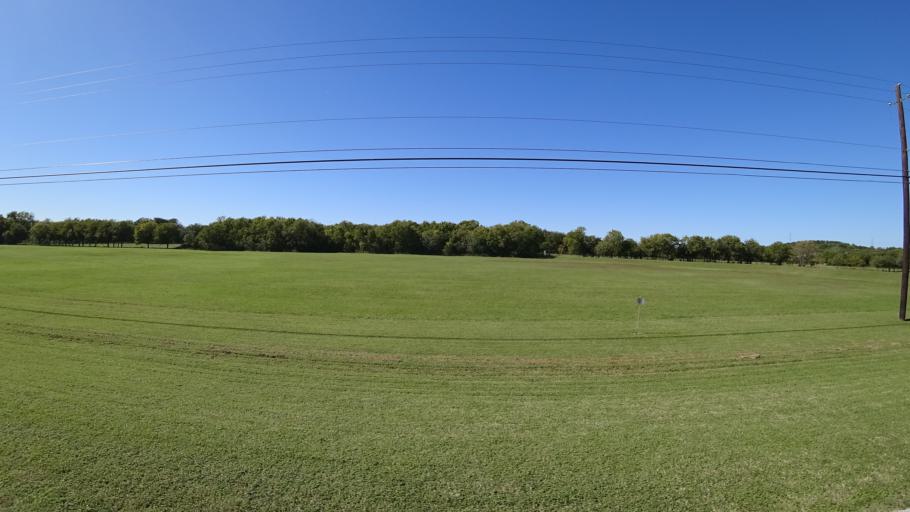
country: US
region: Texas
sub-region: Travis County
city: Hornsby Bend
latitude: 30.2747
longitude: -97.6444
